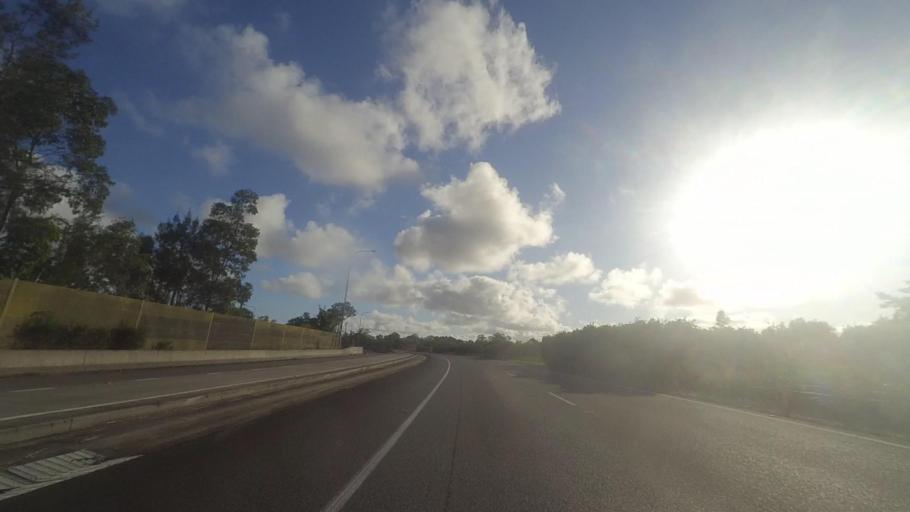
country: AU
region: New South Wales
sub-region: Great Lakes
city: Nabiac
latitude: -32.0975
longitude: 152.3770
